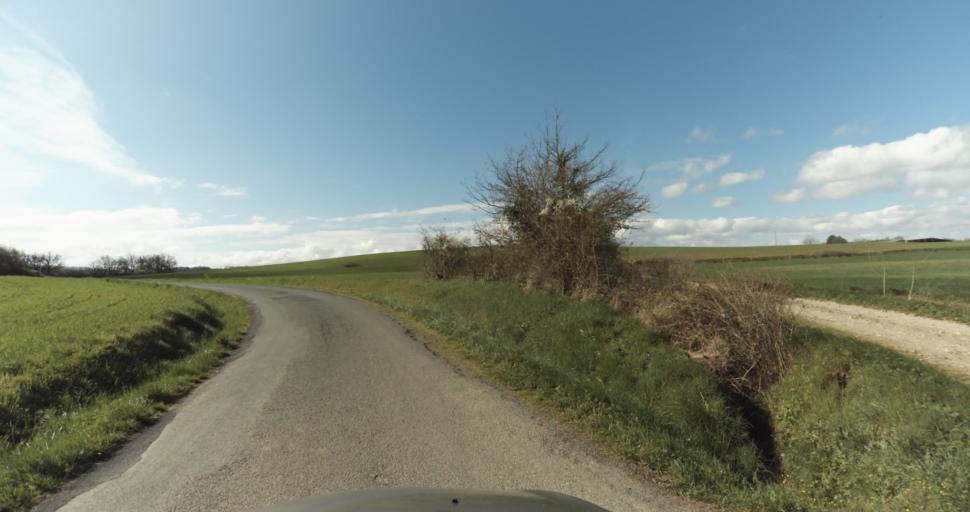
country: FR
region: Midi-Pyrenees
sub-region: Departement du Tarn
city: Puygouzon
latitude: 43.8821
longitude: 2.1819
